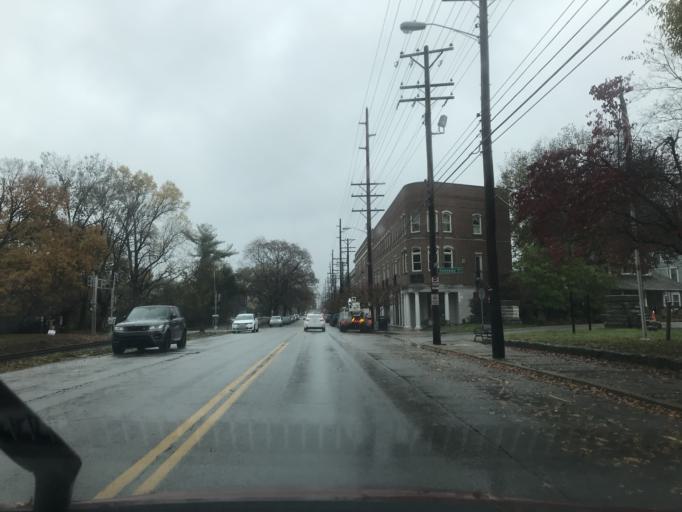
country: US
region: Kentucky
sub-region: Jefferson County
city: Indian Hills
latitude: 38.2547
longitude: -85.6892
